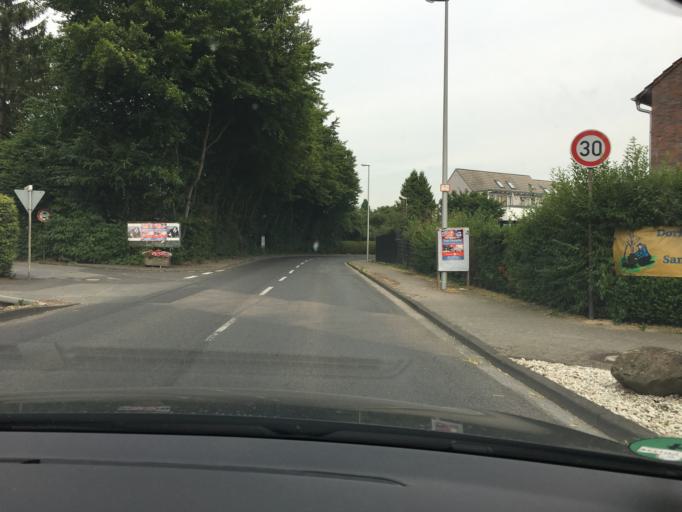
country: DE
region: North Rhine-Westphalia
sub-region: Regierungsbezirk Koln
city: Pulheim
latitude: 50.9594
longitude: 6.7634
